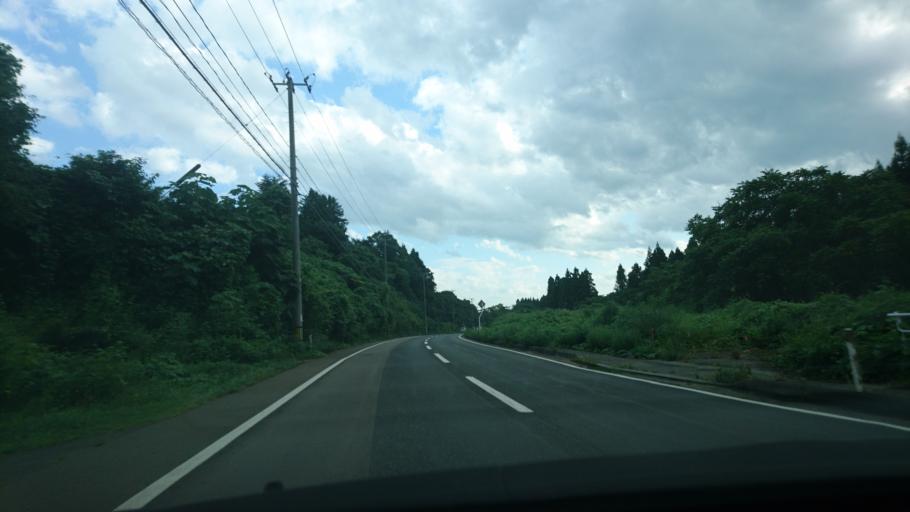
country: JP
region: Iwate
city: Kitakami
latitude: 39.2591
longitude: 141.1230
